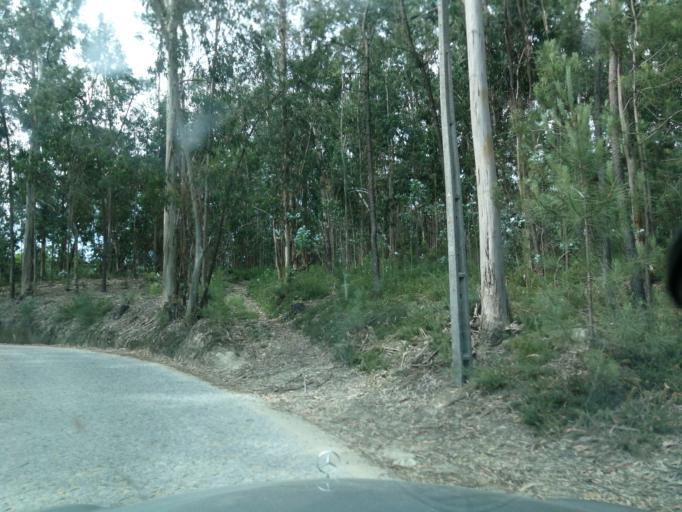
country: PT
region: Braga
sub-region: Braga
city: Oliveira
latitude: 41.4740
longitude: -8.4797
